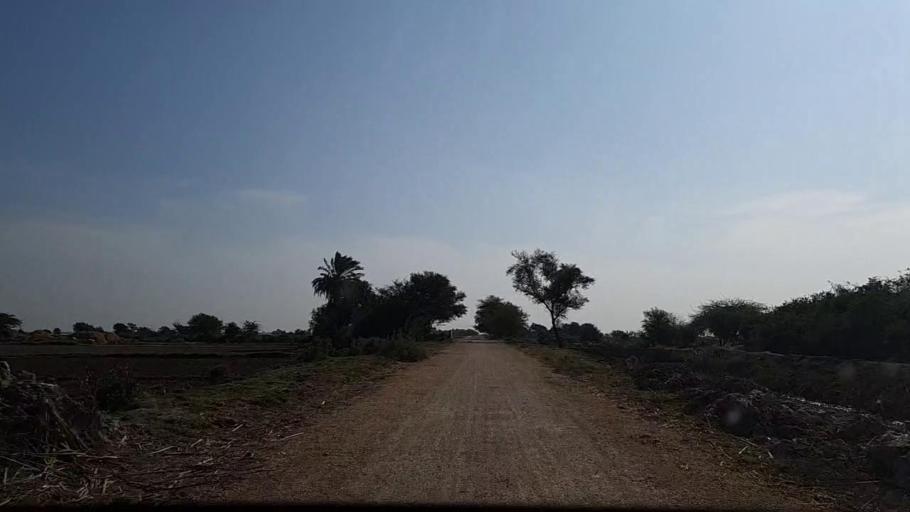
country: PK
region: Sindh
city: Daro Mehar
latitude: 24.7197
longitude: 68.1157
